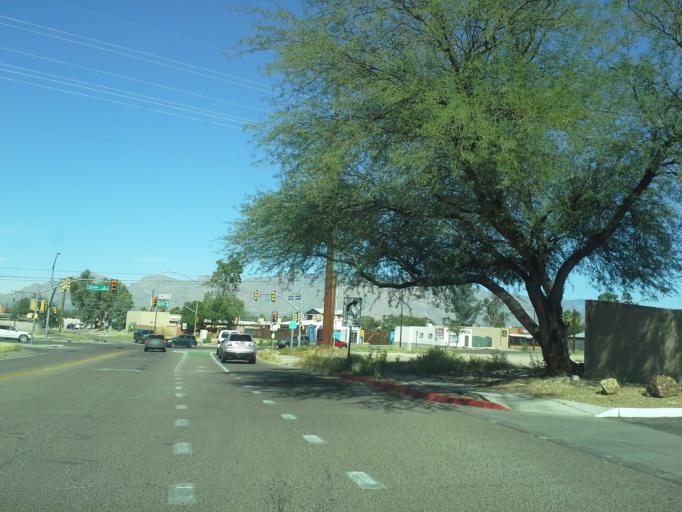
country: US
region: Arizona
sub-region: Pima County
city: Tucson
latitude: 32.2496
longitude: -110.9679
